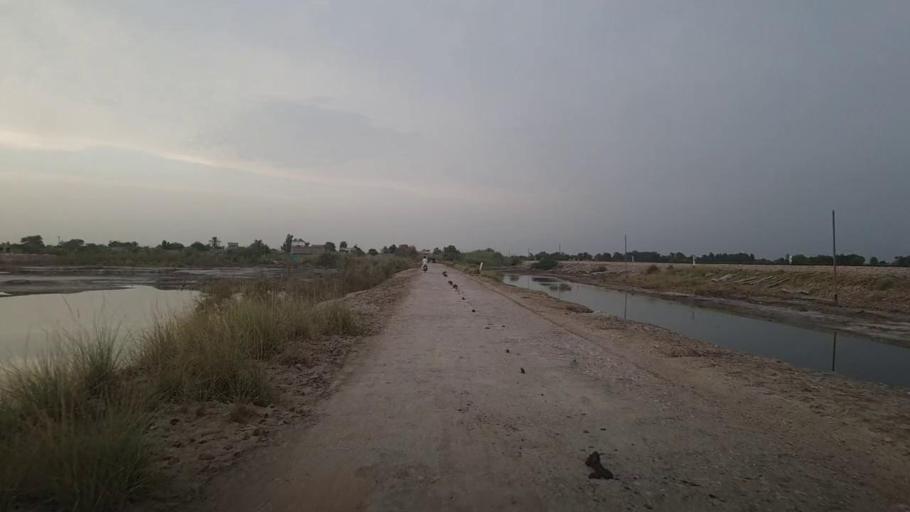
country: PK
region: Sindh
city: Karaundi
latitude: 27.0002
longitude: 68.3516
